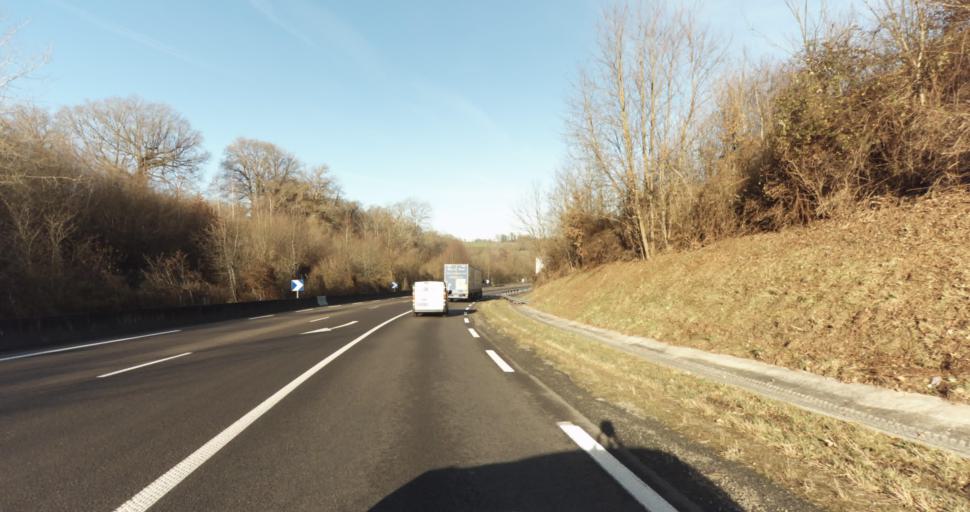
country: FR
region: Limousin
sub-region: Departement de la Haute-Vienne
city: Saint-Priest-sous-Aixe
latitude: 45.7969
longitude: 1.1089
